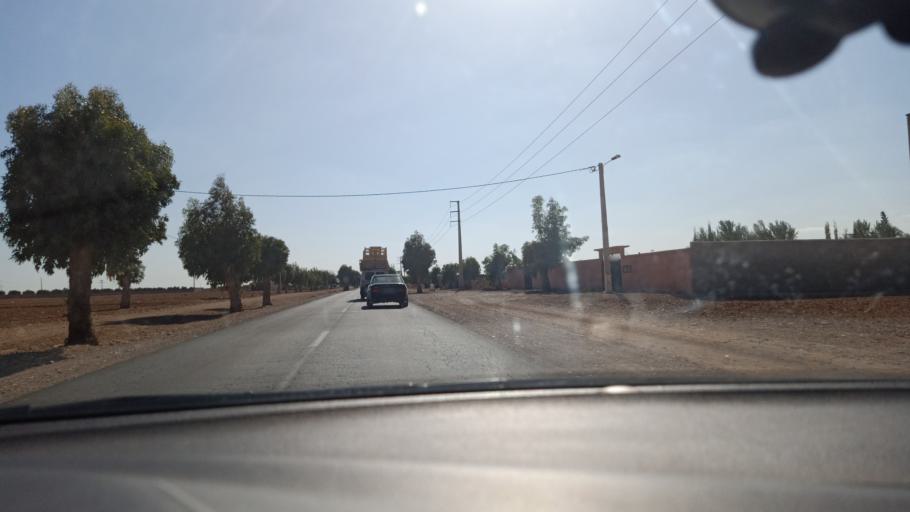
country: MA
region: Doukkala-Abda
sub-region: Safi
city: Youssoufia
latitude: 32.1009
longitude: -8.6127
